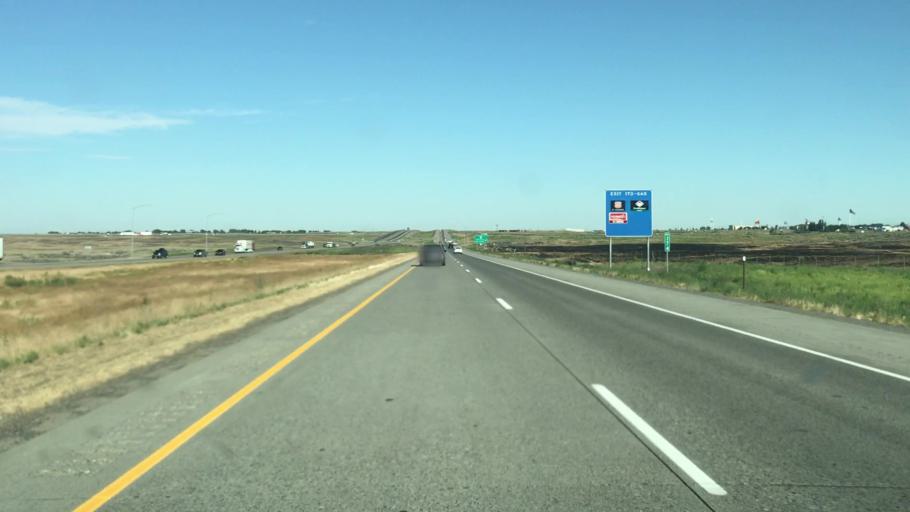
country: US
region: Idaho
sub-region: Twin Falls County
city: Twin Falls
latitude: 42.6360
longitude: -114.4275
